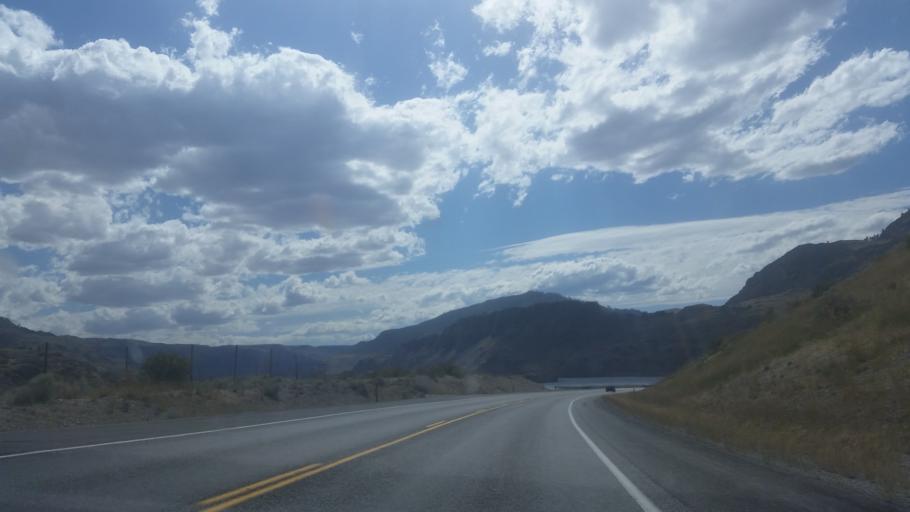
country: US
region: Washington
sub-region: Chelan County
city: Chelan
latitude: 47.8564
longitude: -119.9368
